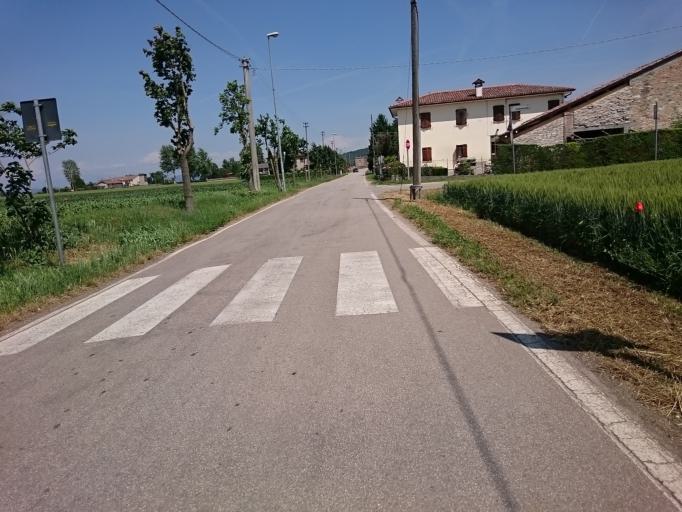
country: IT
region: Veneto
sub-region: Provincia di Padova
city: Lozzo Atestino
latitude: 45.2610
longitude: 11.6189
